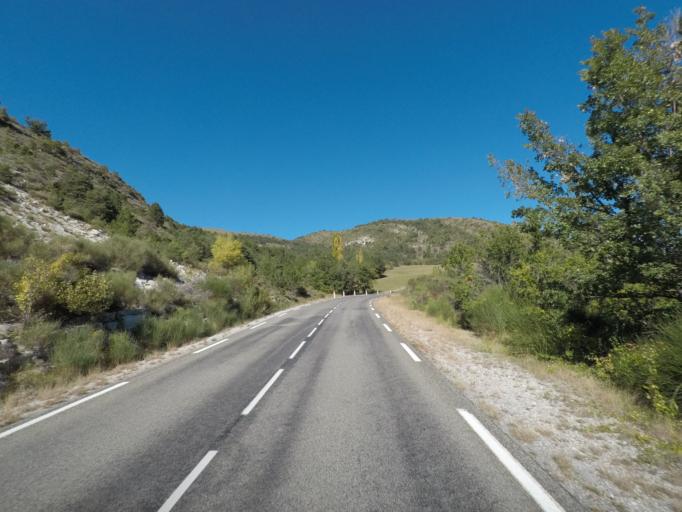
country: FR
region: Provence-Alpes-Cote d'Azur
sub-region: Departement des Hautes-Alpes
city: Serres
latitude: 44.3934
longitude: 5.4946
